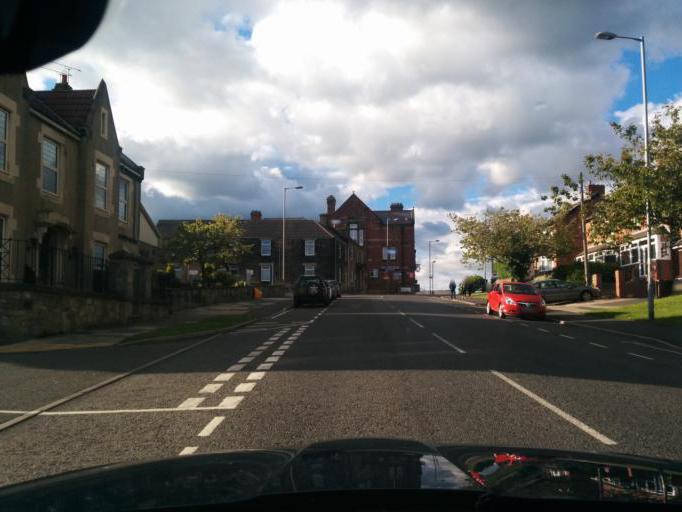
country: GB
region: England
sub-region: Northumberland
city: Bedlington
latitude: 55.1302
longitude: -1.6006
